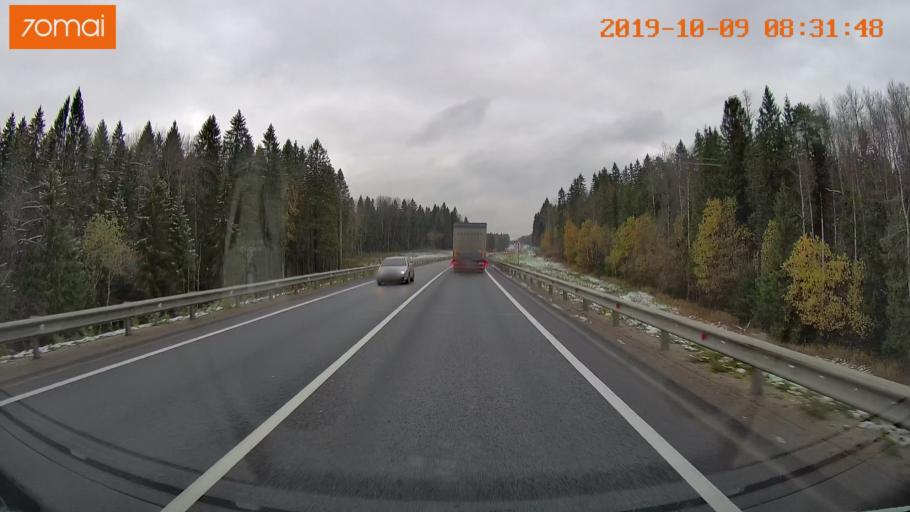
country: RU
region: Vologda
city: Gryazovets
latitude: 58.8585
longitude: 40.1997
